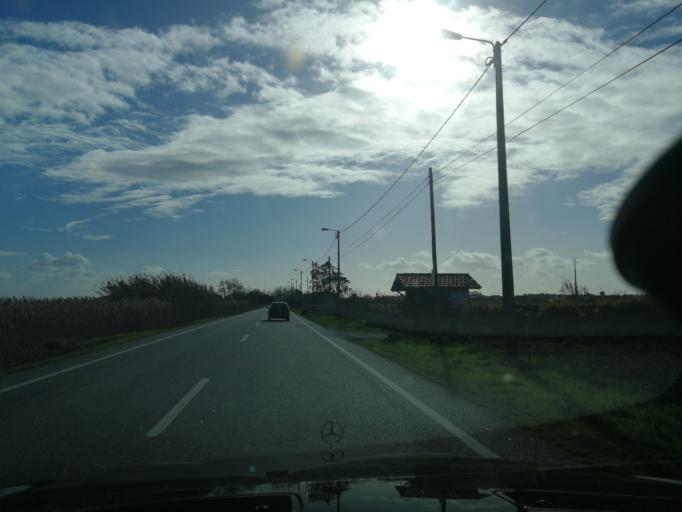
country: PT
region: Aveiro
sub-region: Estarreja
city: Pardilho
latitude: 40.8034
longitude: -8.6733
